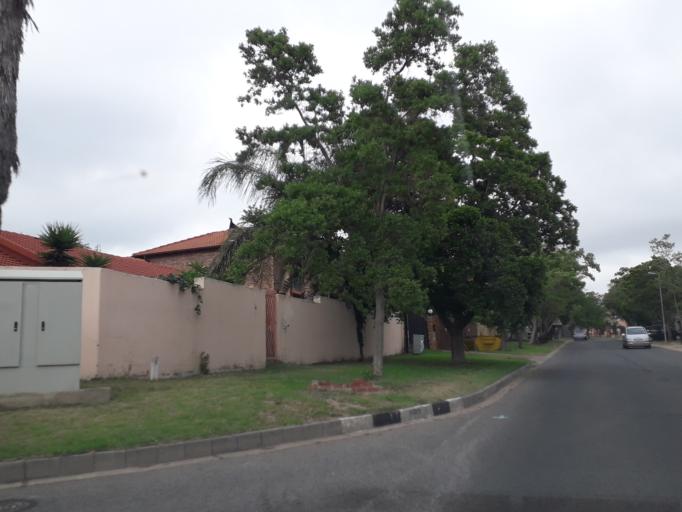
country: ZA
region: Gauteng
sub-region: City of Johannesburg Metropolitan Municipality
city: Roodepoort
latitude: -26.1048
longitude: 27.9530
